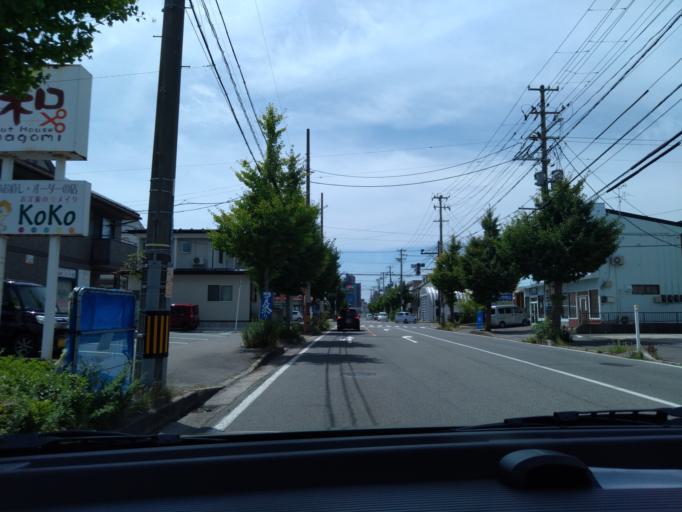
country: JP
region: Akita
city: Akita
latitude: 39.7122
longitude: 140.1349
